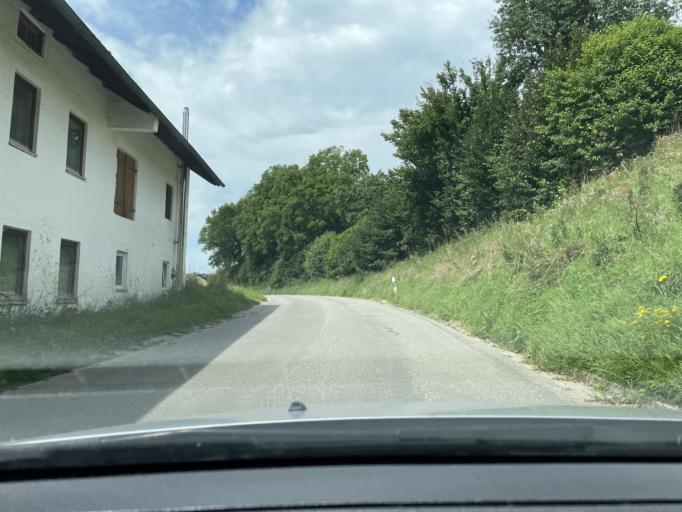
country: DE
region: Bavaria
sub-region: Lower Bavaria
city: Geisenhausen
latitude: 48.4398
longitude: 12.2744
